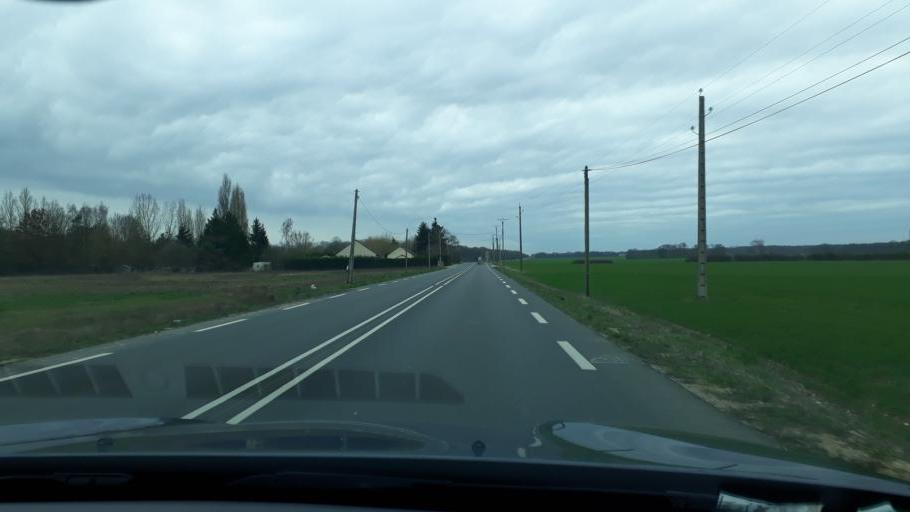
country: FR
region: Centre
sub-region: Departement du Loiret
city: Chanteau
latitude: 48.0316
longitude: 1.9740
